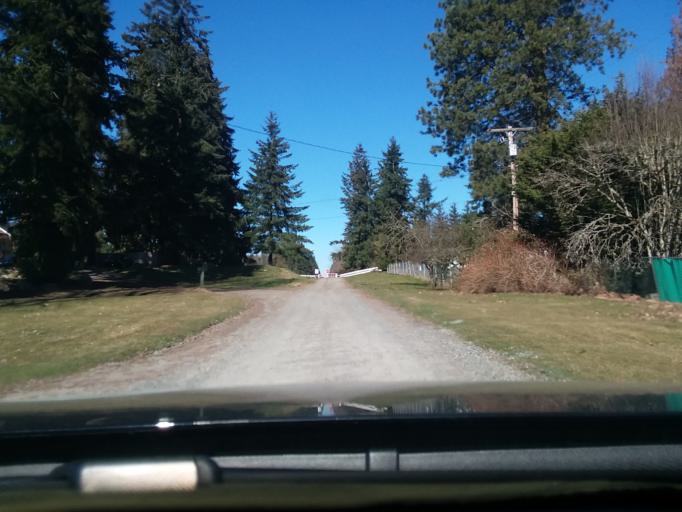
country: US
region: Washington
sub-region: Pierce County
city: Summit
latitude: 47.1638
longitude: -122.3373
